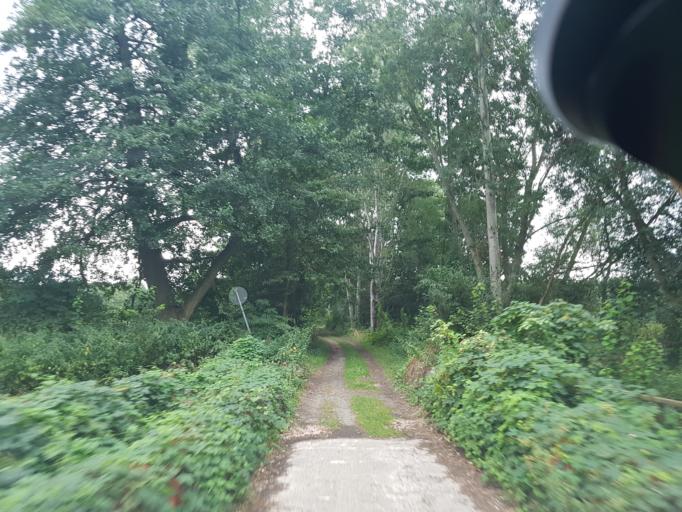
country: DE
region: Brandenburg
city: Ruckersdorf
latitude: 51.6011
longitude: 13.5694
